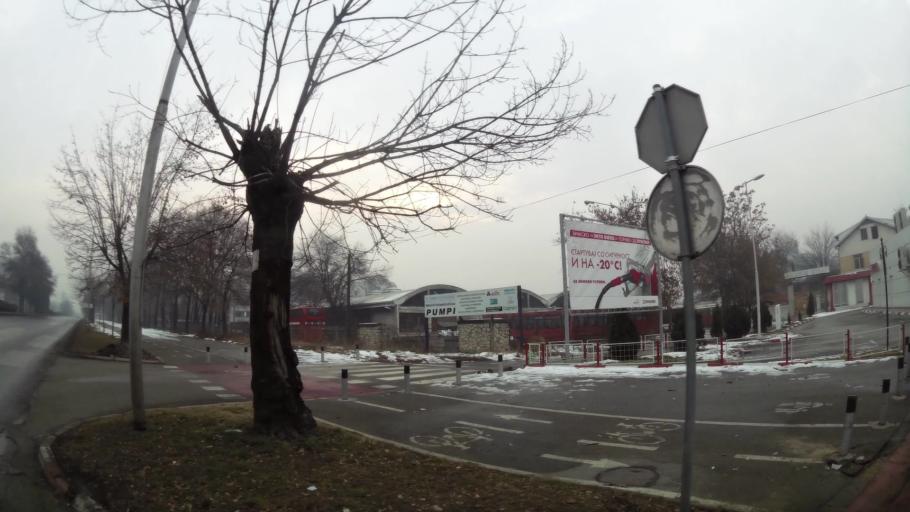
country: MK
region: Cair
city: Cair
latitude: 42.0012
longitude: 21.4627
